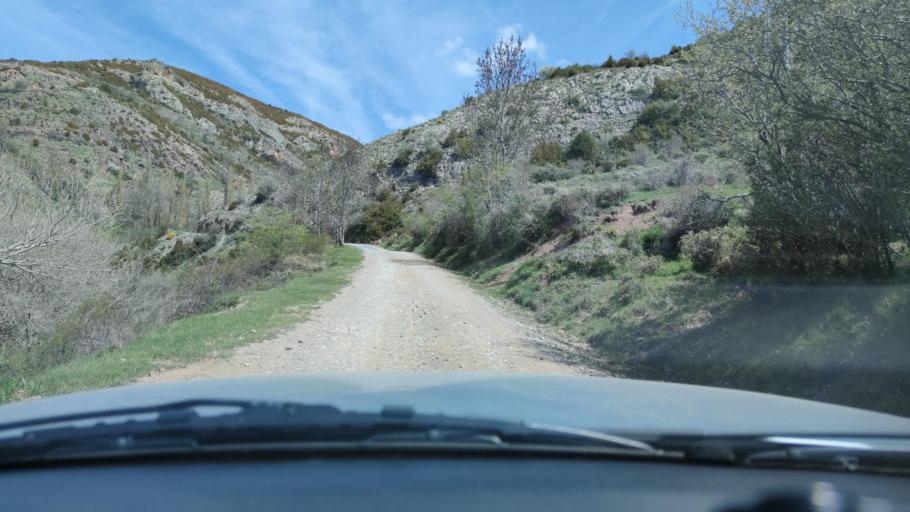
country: ES
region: Catalonia
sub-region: Provincia de Lleida
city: Sort
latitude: 42.2971
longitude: 1.1799
